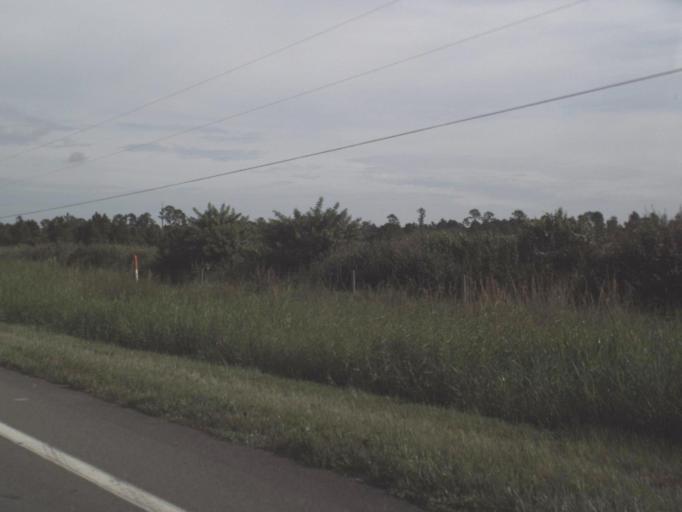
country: US
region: Florida
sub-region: Lee County
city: Olga
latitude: 26.8635
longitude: -81.7597
